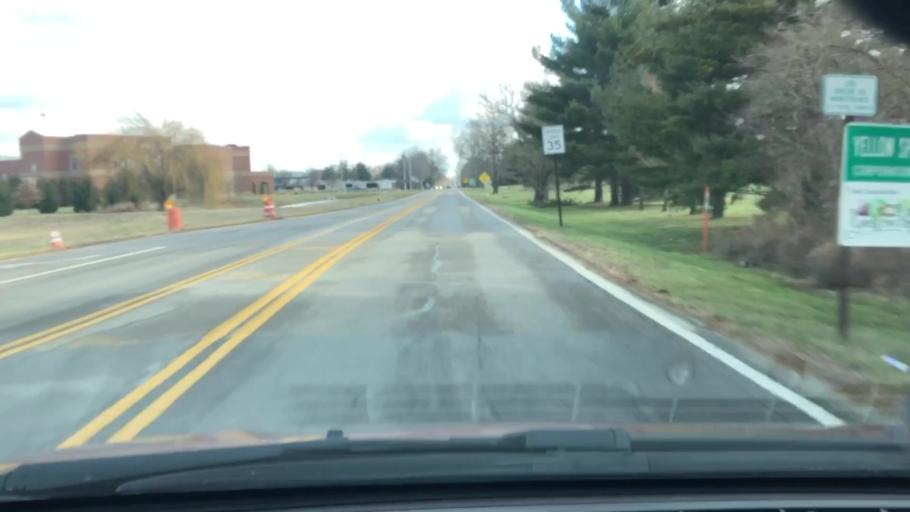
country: US
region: Ohio
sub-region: Greene County
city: Yellow Springs
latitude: 39.8021
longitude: -83.9106
